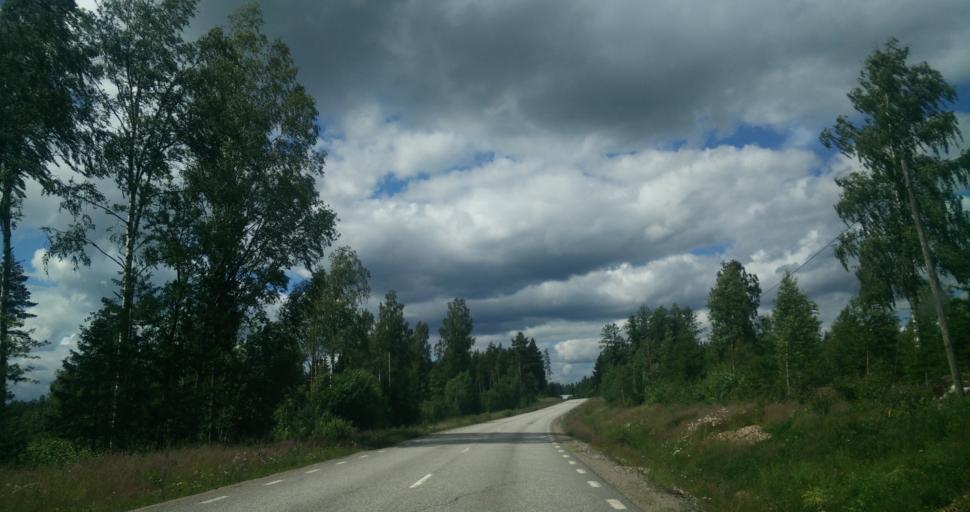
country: SE
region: Gaevleborg
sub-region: Nordanstigs Kommun
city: Bergsjoe
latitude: 62.0885
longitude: 16.7820
